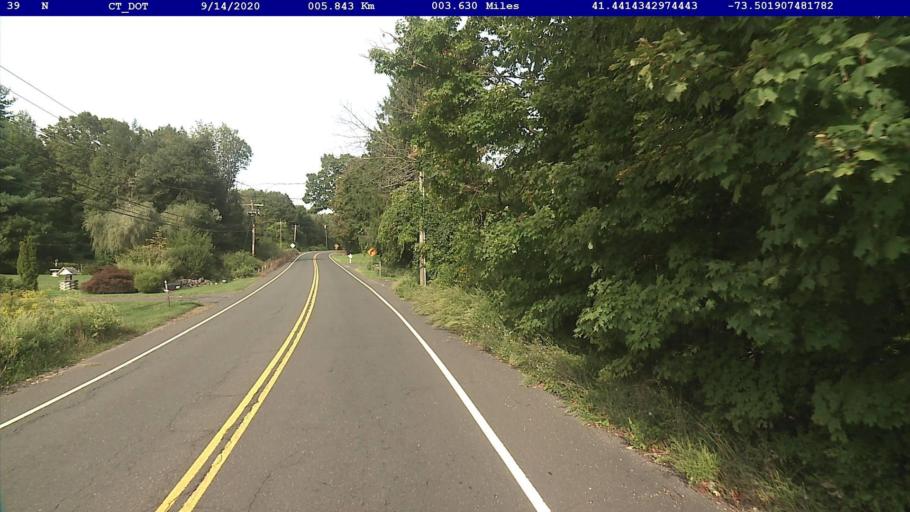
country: US
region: New York
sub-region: Putnam County
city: Putnam Lake
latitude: 41.4414
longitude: -73.5019
